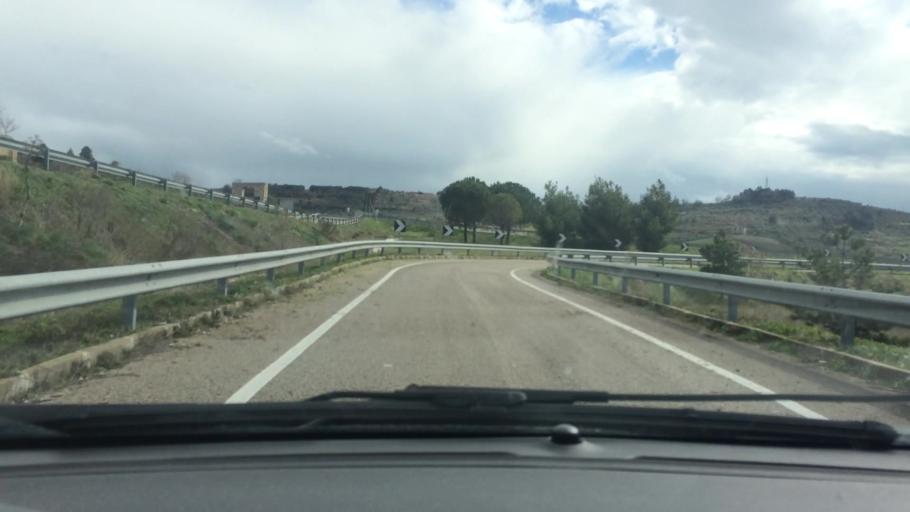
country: IT
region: Apulia
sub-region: Provincia di Bari
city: Gravina in Puglia
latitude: 40.8060
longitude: 16.4204
